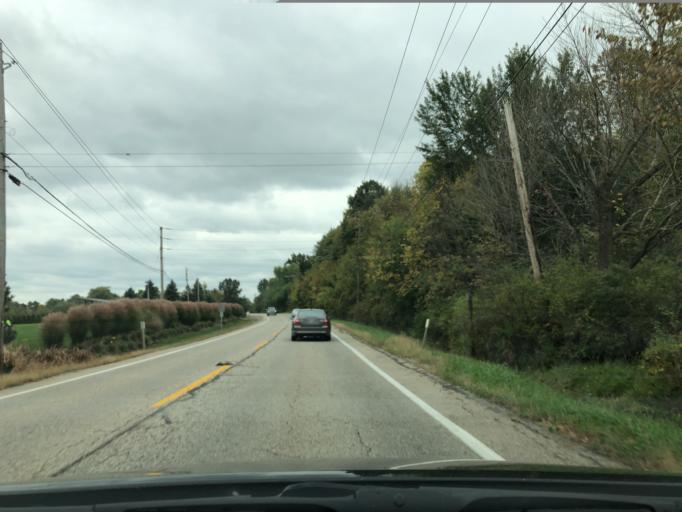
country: US
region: Ohio
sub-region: Summit County
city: Cuyahoga Falls
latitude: 41.1751
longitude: -81.4944
